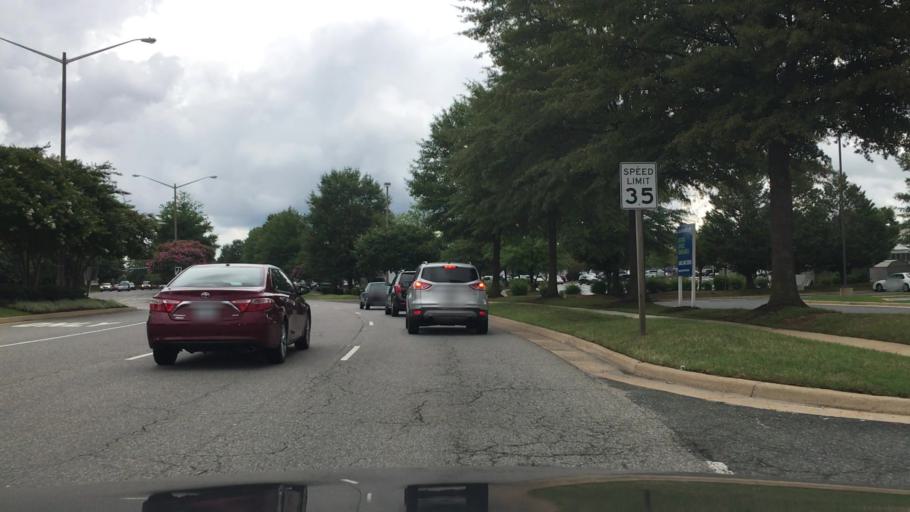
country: US
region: Virginia
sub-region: Stafford County
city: Falmouth
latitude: 38.2995
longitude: -77.5102
